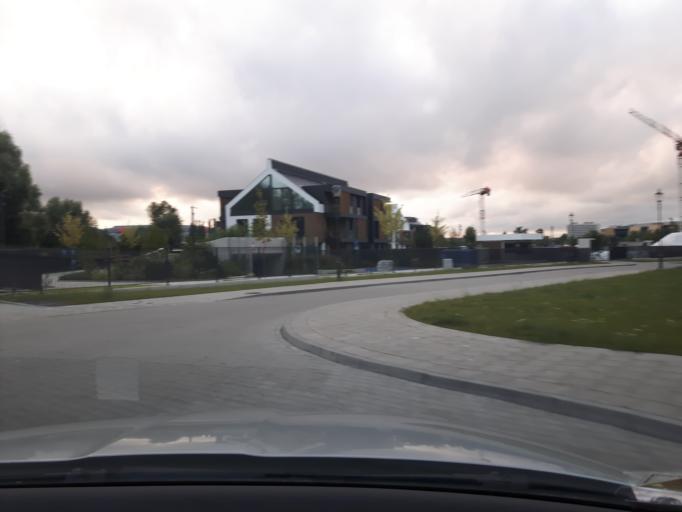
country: PL
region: Pomeranian Voivodeship
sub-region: Sopot
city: Sopot
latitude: 54.4233
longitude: 18.5902
